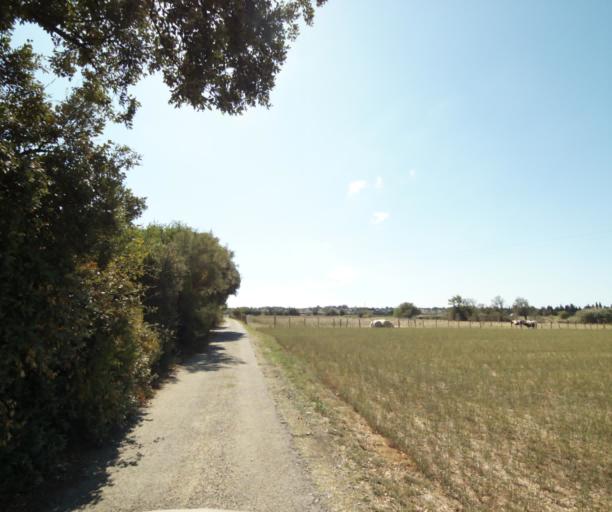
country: FR
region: Languedoc-Roussillon
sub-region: Departement du Gard
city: Bouillargues
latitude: 43.8127
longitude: 4.4218
